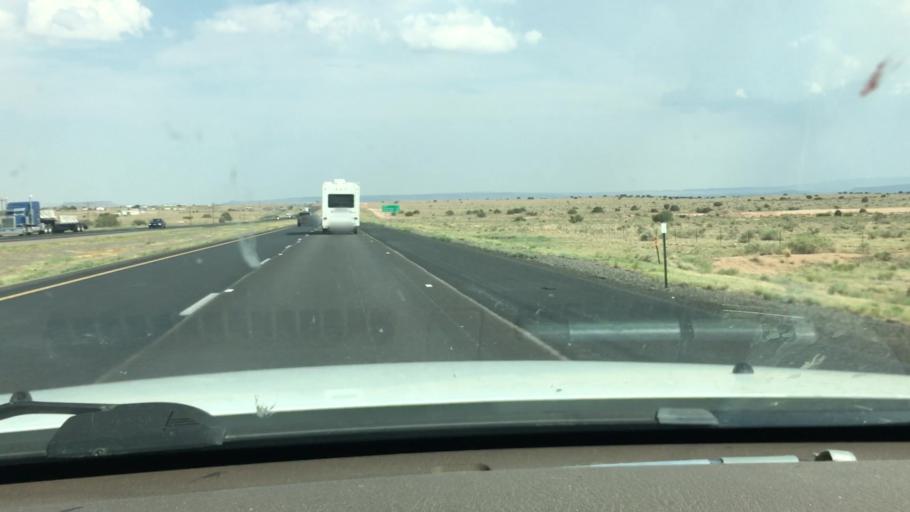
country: US
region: New Mexico
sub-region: Cibola County
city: Laguna
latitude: 35.0063
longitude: -107.3157
